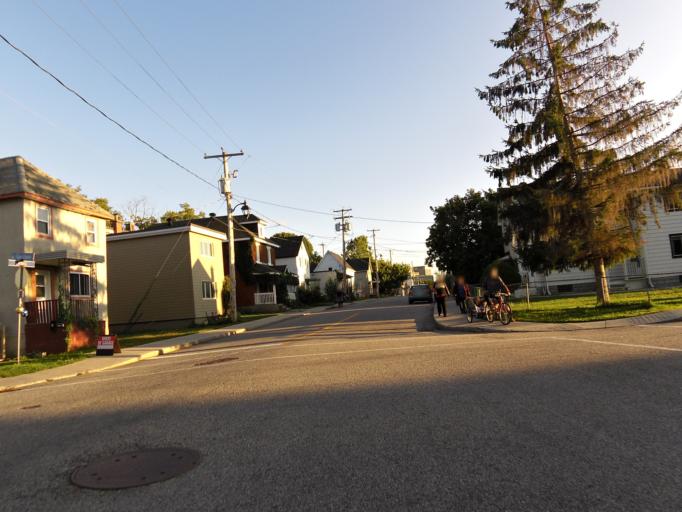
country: CA
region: Ontario
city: Ottawa
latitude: 45.4358
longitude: -75.7148
